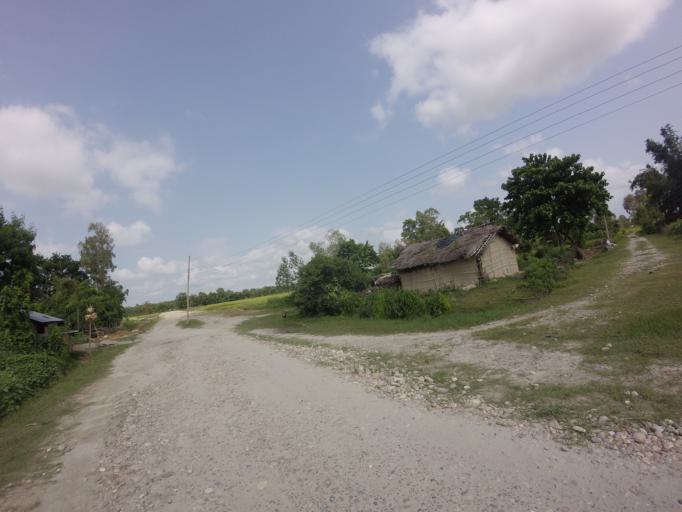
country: NP
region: Far Western
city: Tikapur
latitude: 28.4420
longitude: 81.0711
